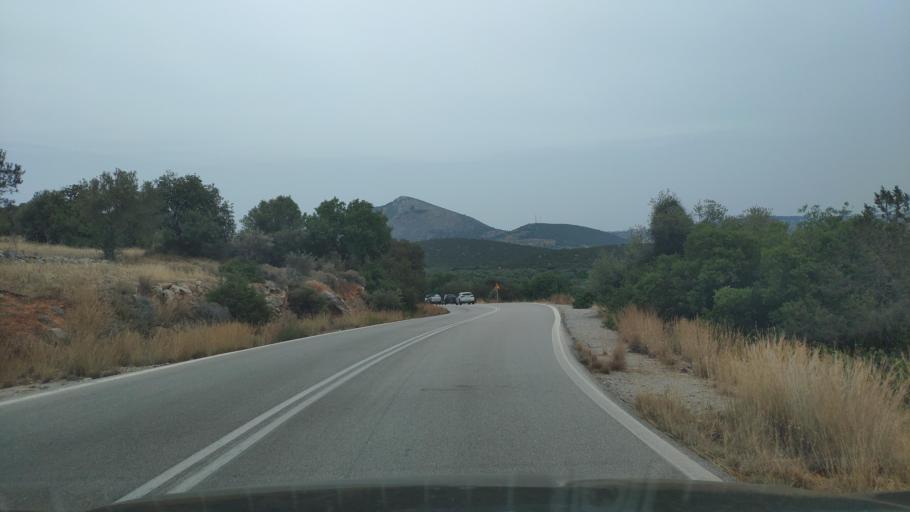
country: GR
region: Peloponnese
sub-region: Nomos Argolidos
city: Koilas
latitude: 37.4230
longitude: 23.1530
